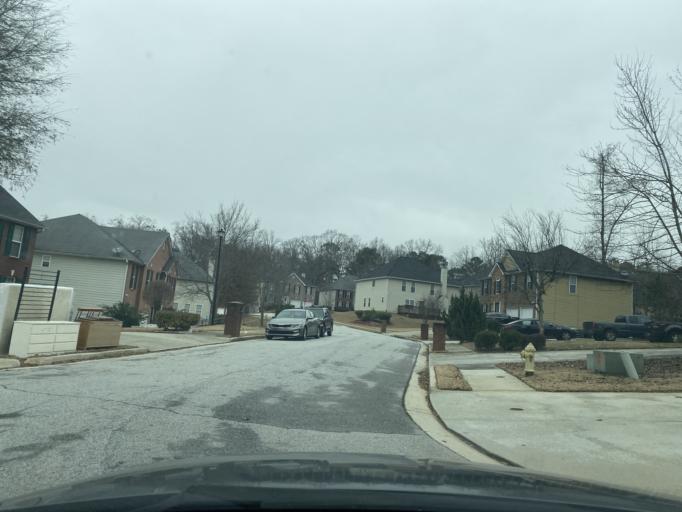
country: US
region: Georgia
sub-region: DeKalb County
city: Pine Mountain
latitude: 33.6890
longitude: -84.1462
